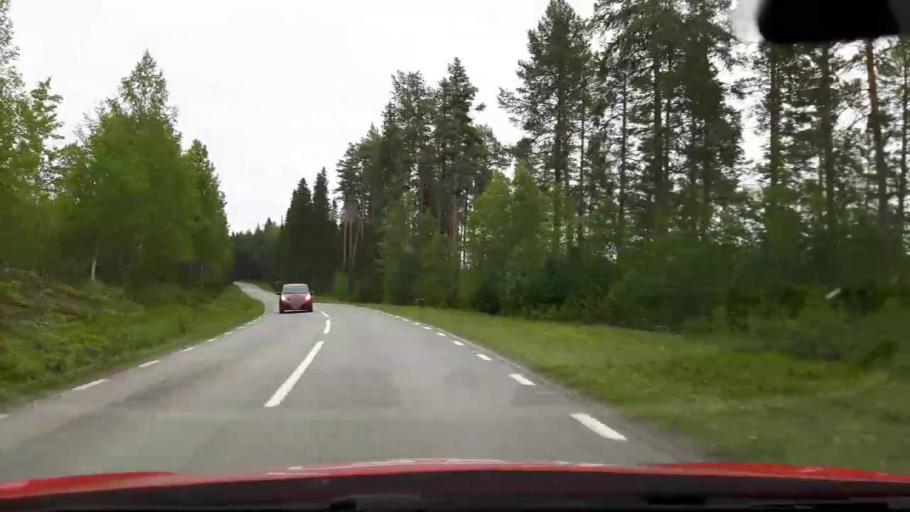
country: SE
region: Jaemtland
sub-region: Stroemsunds Kommun
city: Stroemsund
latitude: 63.4183
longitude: 15.5520
